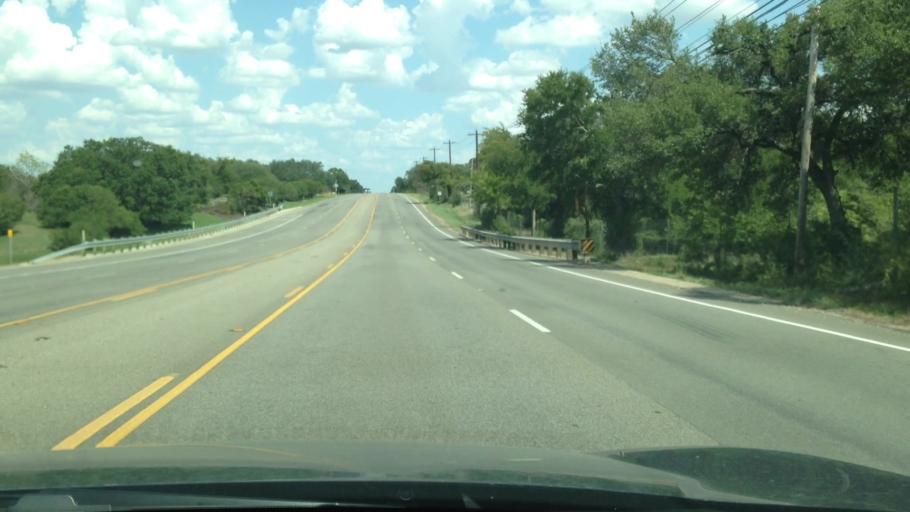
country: US
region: Texas
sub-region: Williamson County
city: Leander
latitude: 30.6363
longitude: -97.7923
